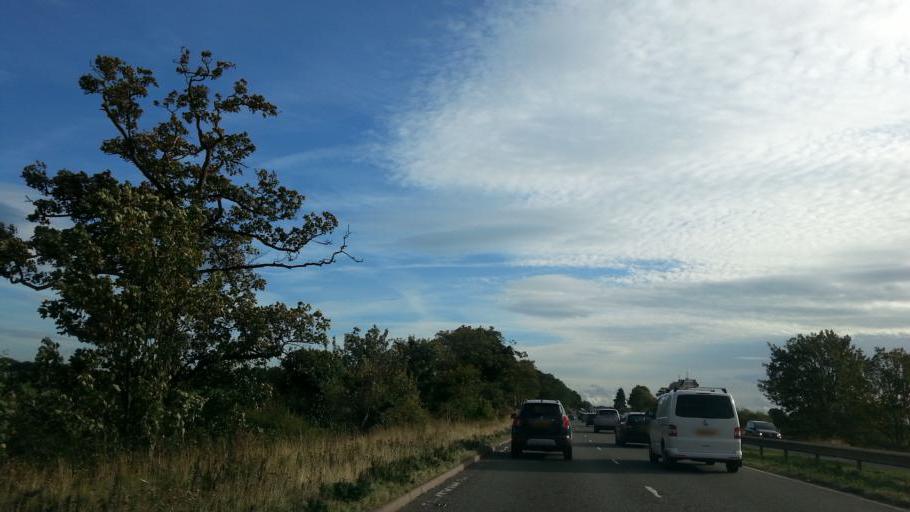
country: GB
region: England
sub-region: Nottinghamshire
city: Babworth
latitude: 53.3403
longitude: -1.0292
